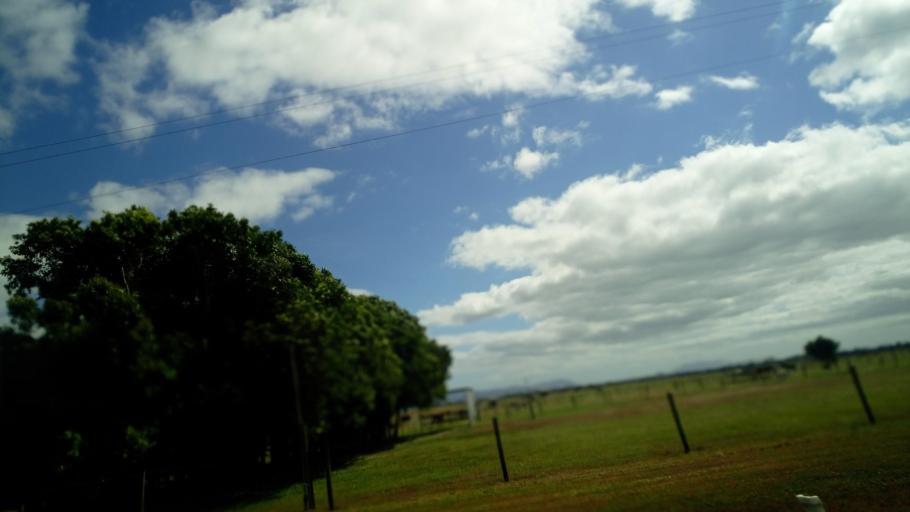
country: AU
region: Queensland
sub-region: Tablelands
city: Mareeba
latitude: -16.9740
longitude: 145.4577
